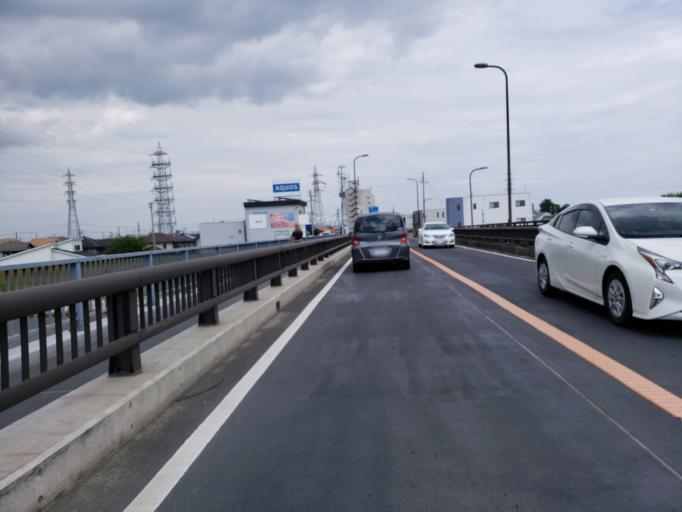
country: JP
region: Hyogo
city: Tatsunocho-tominaga
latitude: 34.7819
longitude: 134.5739
